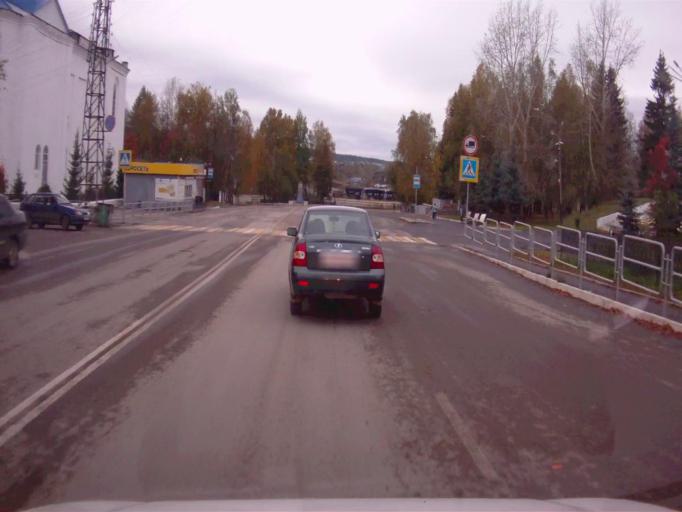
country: RU
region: Chelyabinsk
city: Nyazepetrovsk
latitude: 56.0538
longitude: 59.5960
